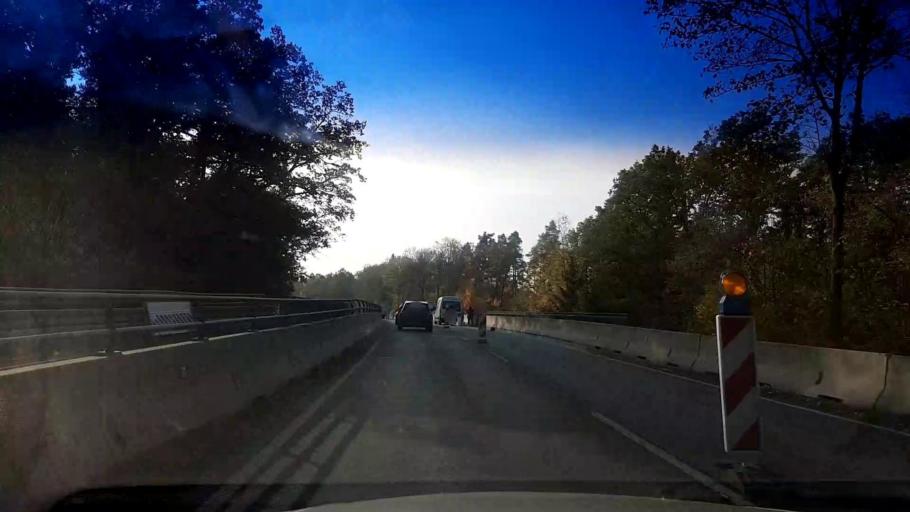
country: DE
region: Bavaria
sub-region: Upper Franconia
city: Neuenmarkt
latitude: 50.0834
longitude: 11.6084
